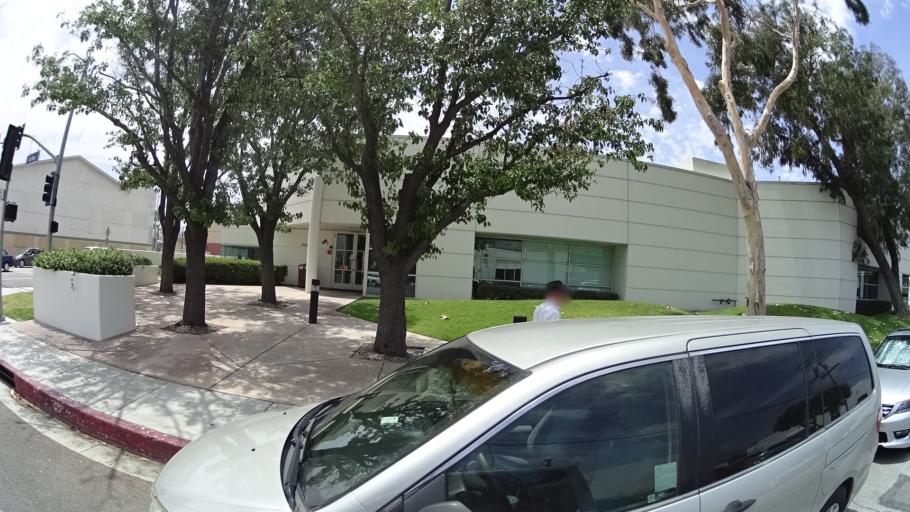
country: US
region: California
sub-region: Los Angeles County
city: North Glendale
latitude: 34.1612
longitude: -118.2835
